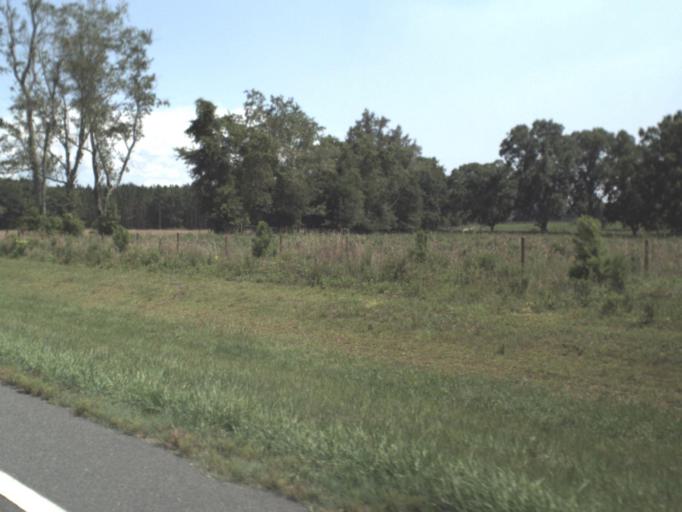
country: US
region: Florida
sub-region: Lafayette County
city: Mayo
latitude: 30.0742
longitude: -83.2072
